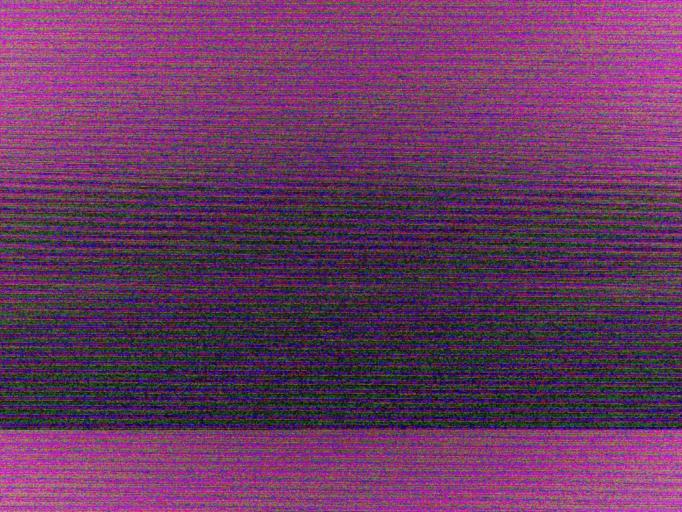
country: US
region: Massachusetts
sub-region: Middlesex County
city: Somerville
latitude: 42.3938
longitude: -71.1055
